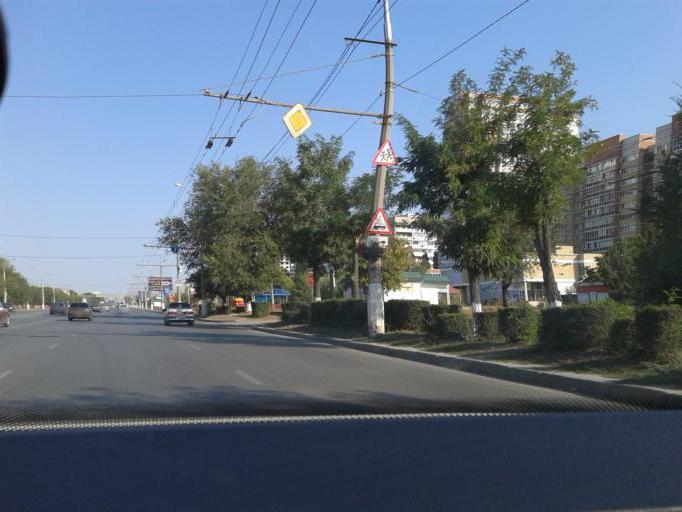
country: RU
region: Volgograd
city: Volgograd
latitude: 48.7444
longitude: 44.4891
